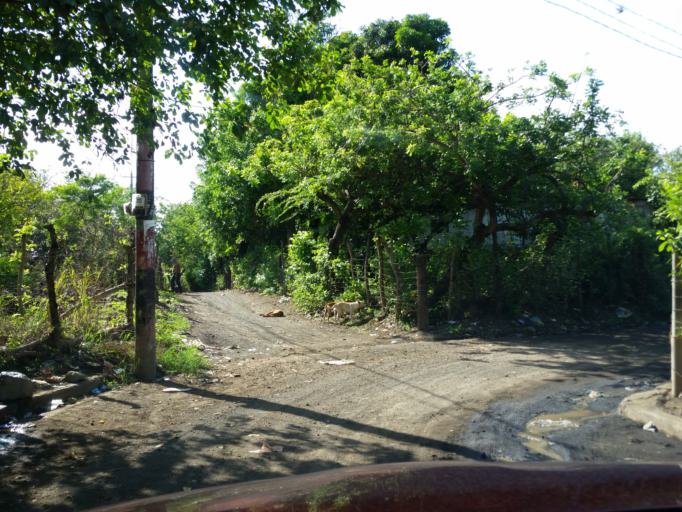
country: NI
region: Managua
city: Managua
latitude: 12.0852
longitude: -86.2614
